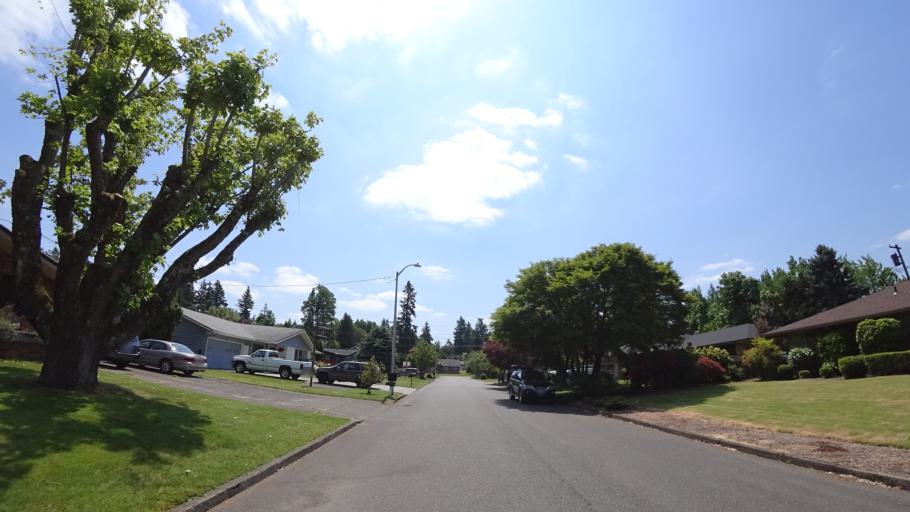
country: US
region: Oregon
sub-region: Multnomah County
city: Fairview
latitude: 45.5347
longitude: -122.5050
